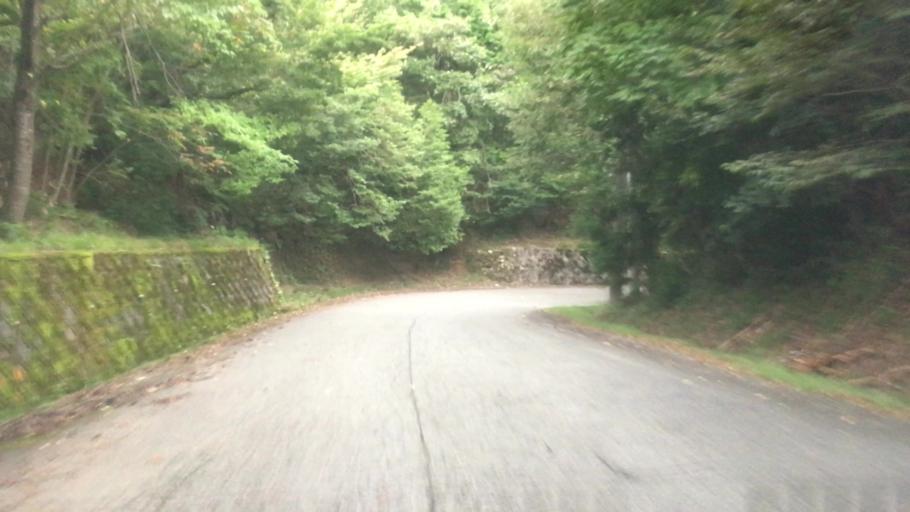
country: JP
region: Hyogo
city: Toyooka
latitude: 35.6204
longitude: 134.8771
